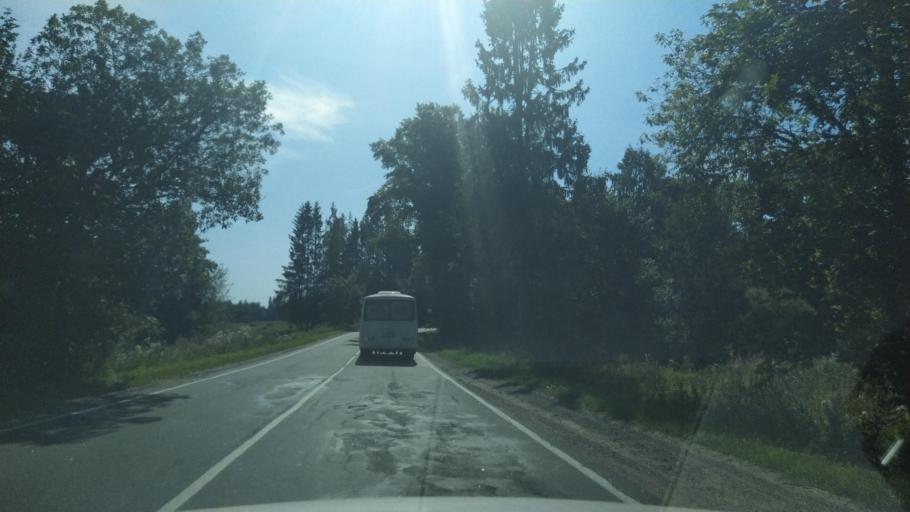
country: RU
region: Leningrad
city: Siverskiy
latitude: 59.3167
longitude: 30.0723
